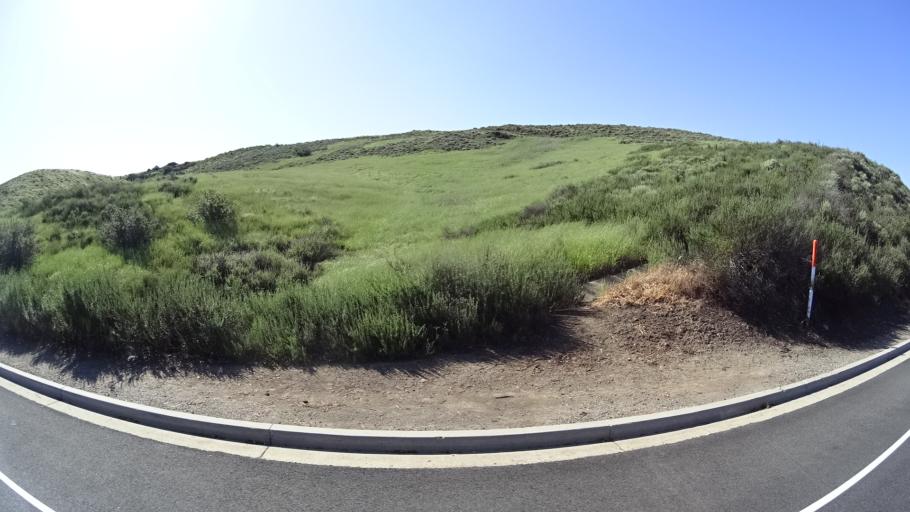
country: US
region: California
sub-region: Ventura County
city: Simi Valley
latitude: 34.2496
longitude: -118.8313
